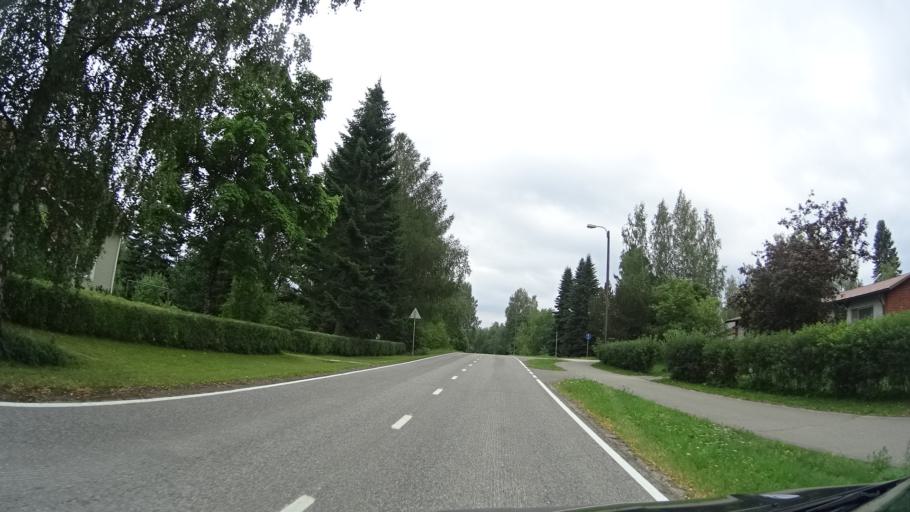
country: FI
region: Southern Savonia
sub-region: Savonlinna
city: Punkaharju
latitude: 61.7516
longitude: 29.3902
